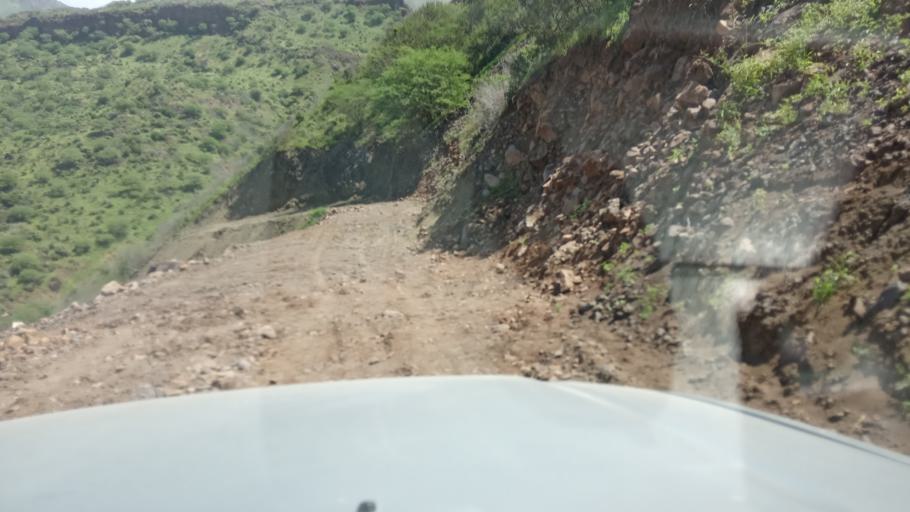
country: CV
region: Santa Catarina
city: Assomada
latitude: 15.1112
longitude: -23.7282
